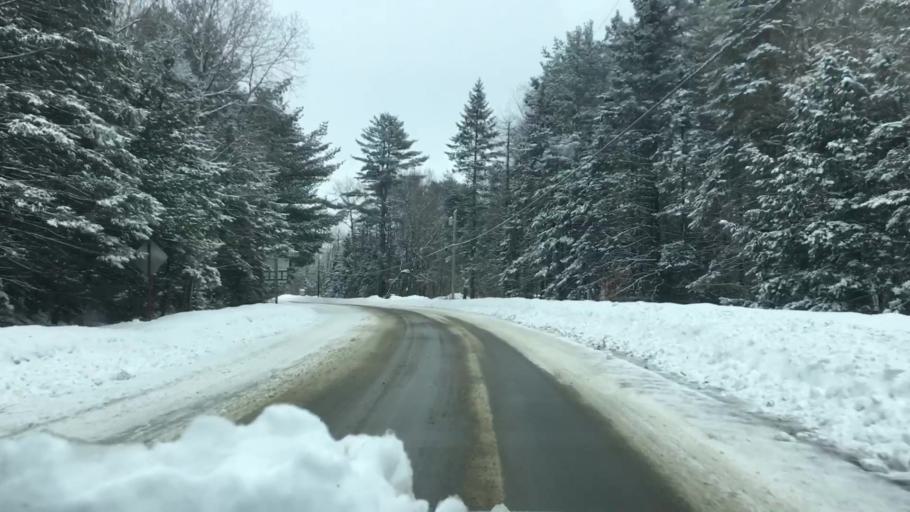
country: US
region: Maine
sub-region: Penobscot County
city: Hudson
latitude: 45.0211
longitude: -68.9136
